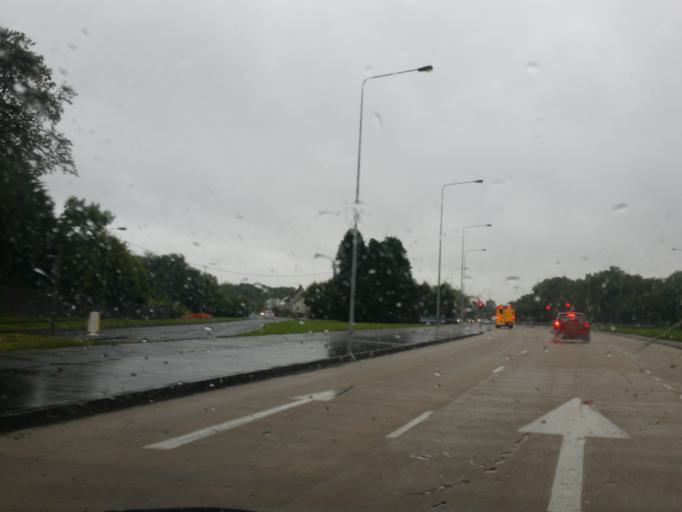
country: GB
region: Northern Ireland
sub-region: North Down District
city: Bangor
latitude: 54.6467
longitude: -5.7158
